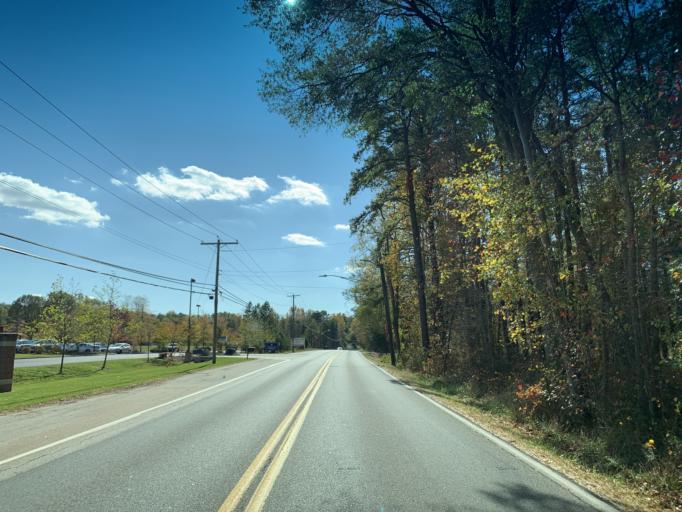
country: US
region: Maryland
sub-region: Anne Arundel County
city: Gambrills
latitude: 39.0993
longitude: -76.6531
